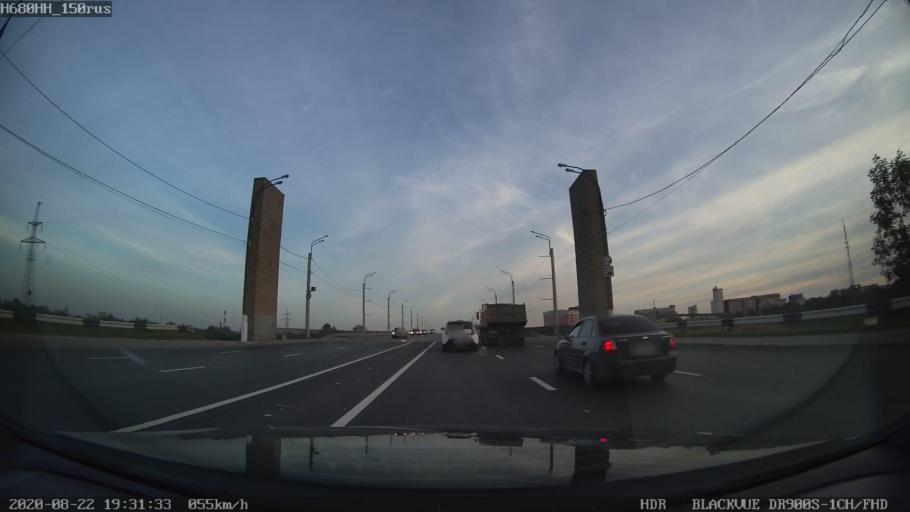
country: RU
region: Tverskaya
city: Tver
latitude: 56.8583
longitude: 35.9444
